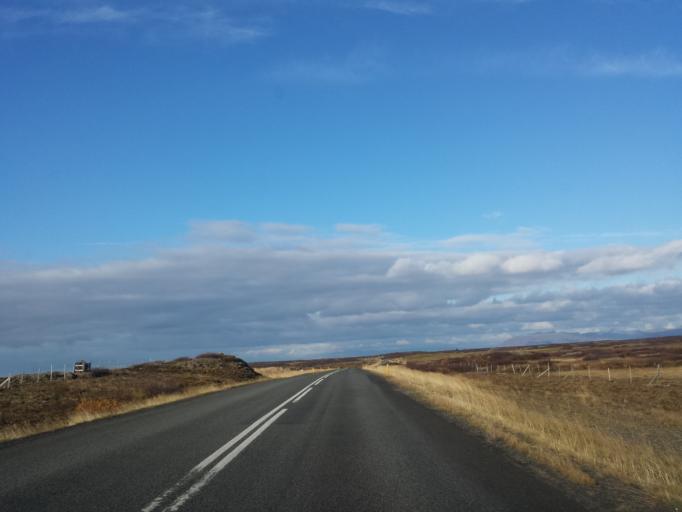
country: IS
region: West
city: Borgarnes
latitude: 64.5612
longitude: -21.9270
